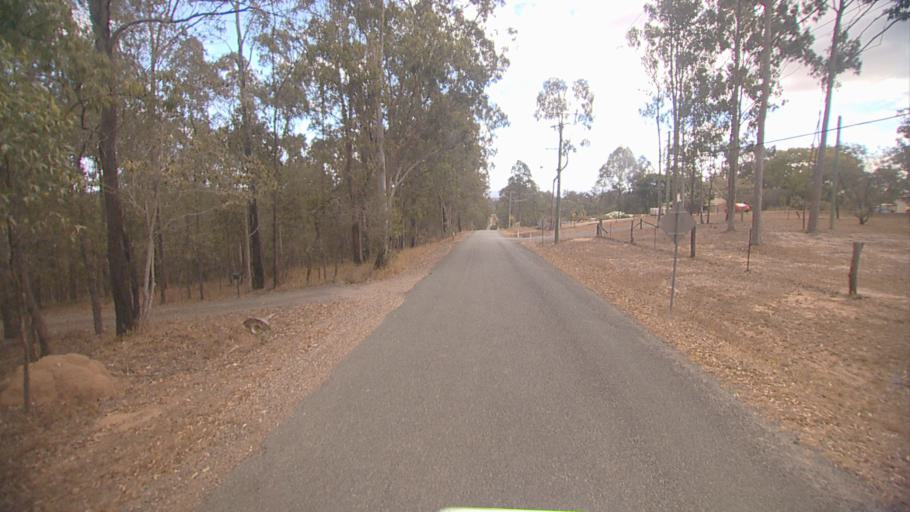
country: AU
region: Queensland
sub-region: Logan
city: Cedar Vale
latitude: -27.8805
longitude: 153.0344
